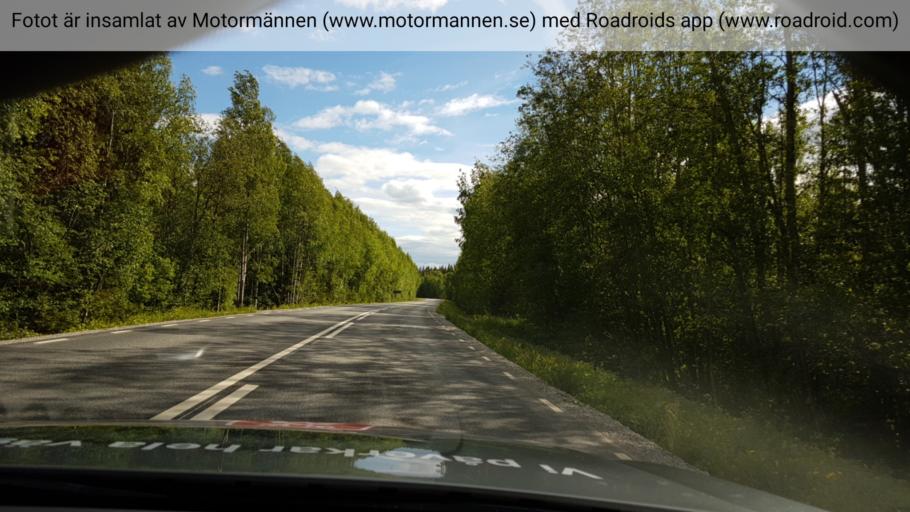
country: SE
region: Jaemtland
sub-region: Stroemsunds Kommun
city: Stroemsund
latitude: 64.1618
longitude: 15.6781
